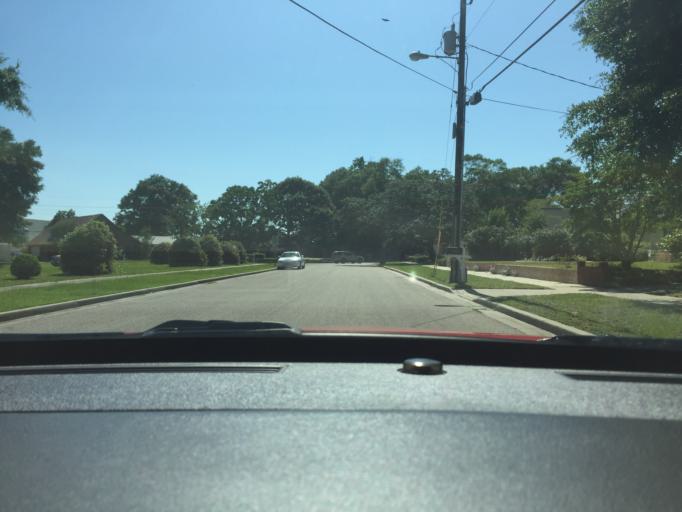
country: US
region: Mississippi
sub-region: Harrison County
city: D'Iberville
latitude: 30.3948
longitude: -88.9889
